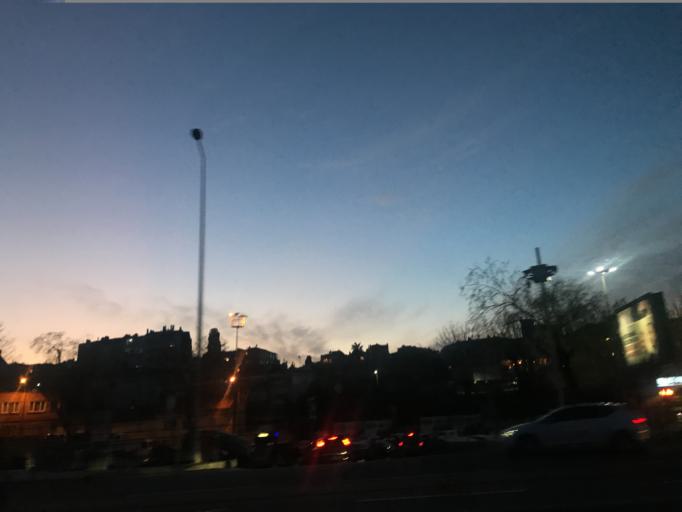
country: TR
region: Istanbul
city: Istanbul
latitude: 40.9986
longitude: 28.9333
